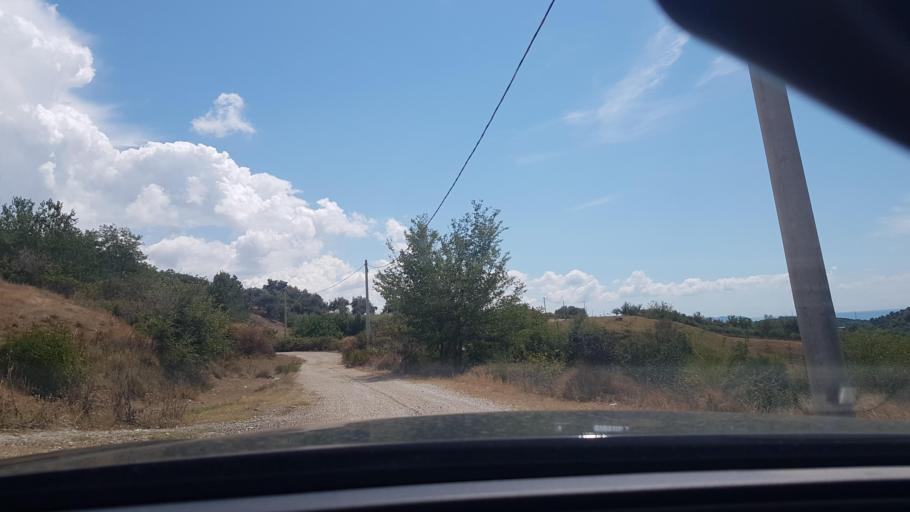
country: AL
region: Tirane
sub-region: Rrethi i Kavajes
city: Golem
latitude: 41.2880
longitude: 19.5486
